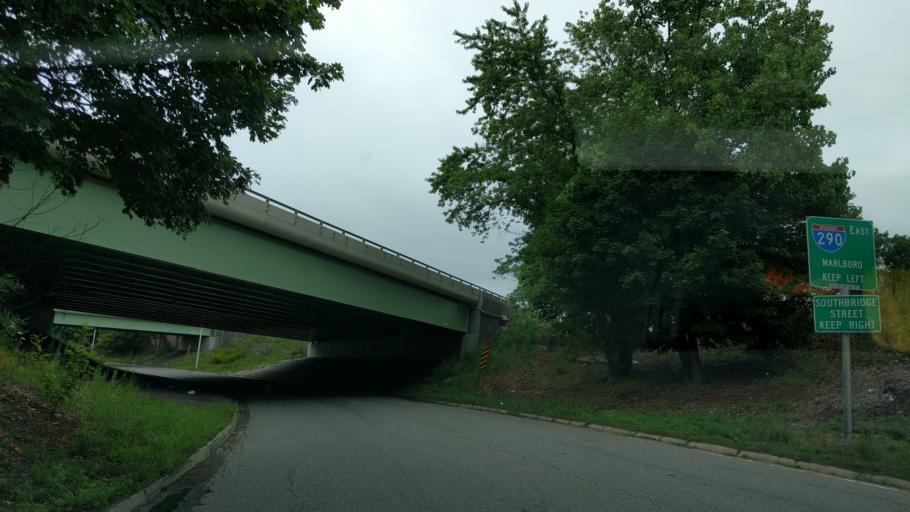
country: US
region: Massachusetts
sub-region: Worcester County
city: Worcester
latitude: 42.2387
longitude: -71.8160
